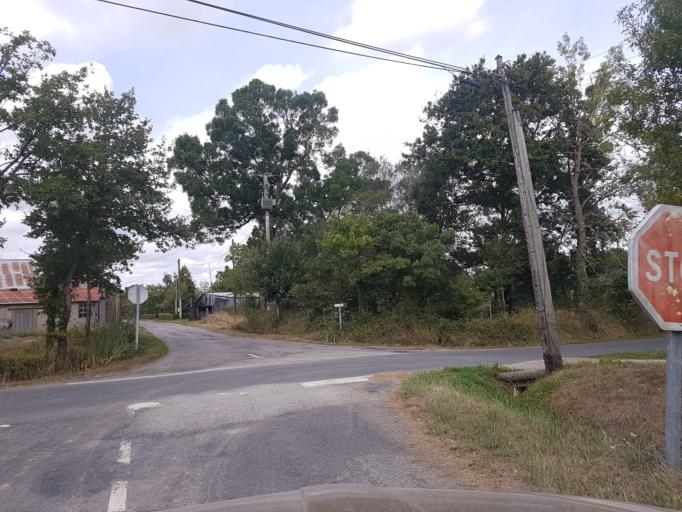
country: FR
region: Pays de la Loire
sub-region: Departement de la Loire-Atlantique
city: Petit-Mars
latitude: 47.4218
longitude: -1.4489
